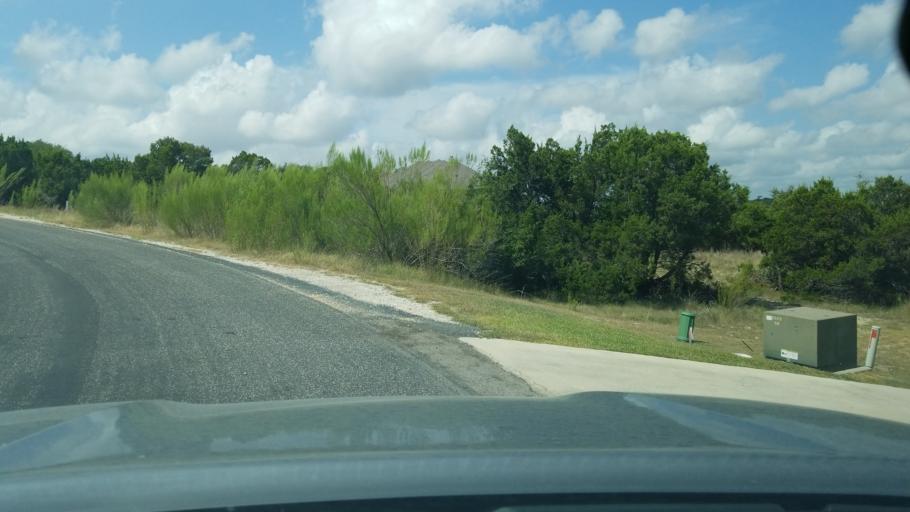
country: US
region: Texas
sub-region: Bexar County
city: Timberwood Park
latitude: 29.6864
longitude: -98.5188
